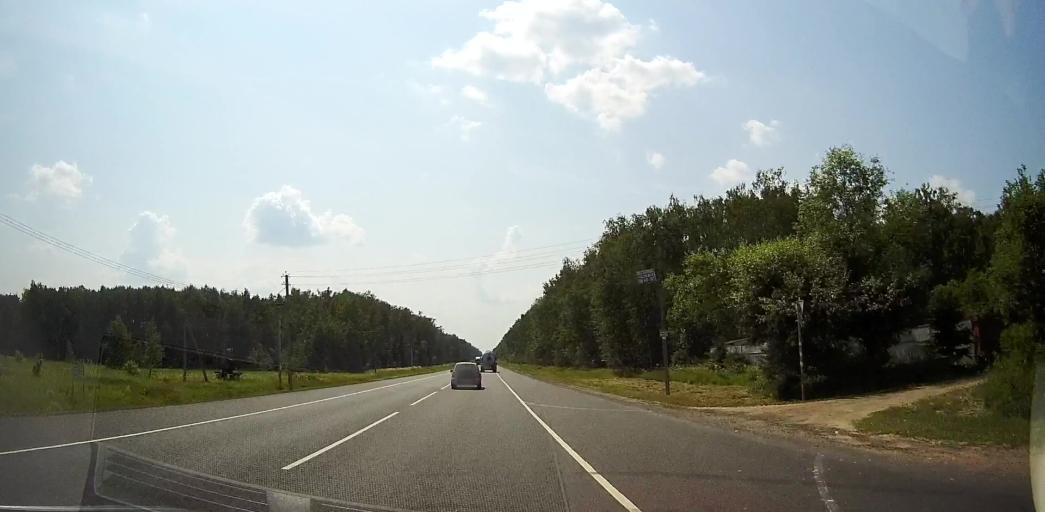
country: RU
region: Moskovskaya
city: Meshcherino
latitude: 55.2204
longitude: 38.3982
